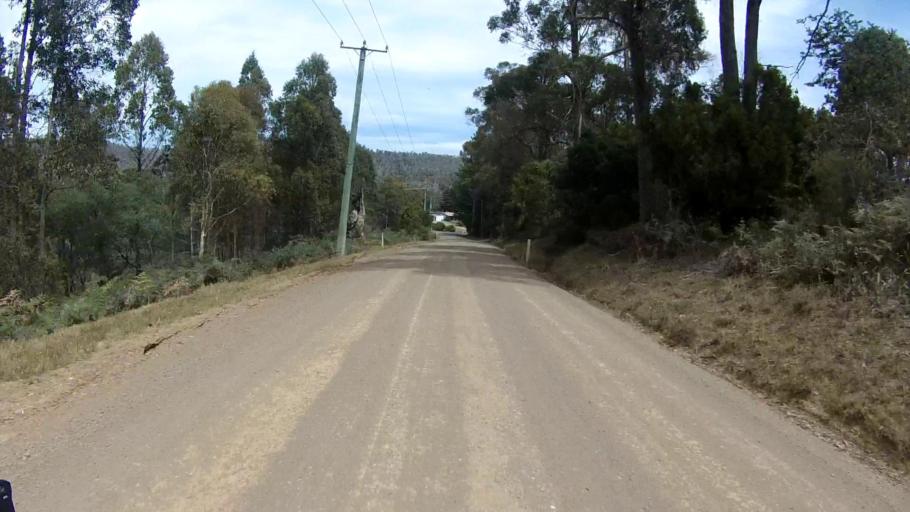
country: AU
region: Tasmania
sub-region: Sorell
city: Sorell
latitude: -42.8026
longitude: 147.6743
